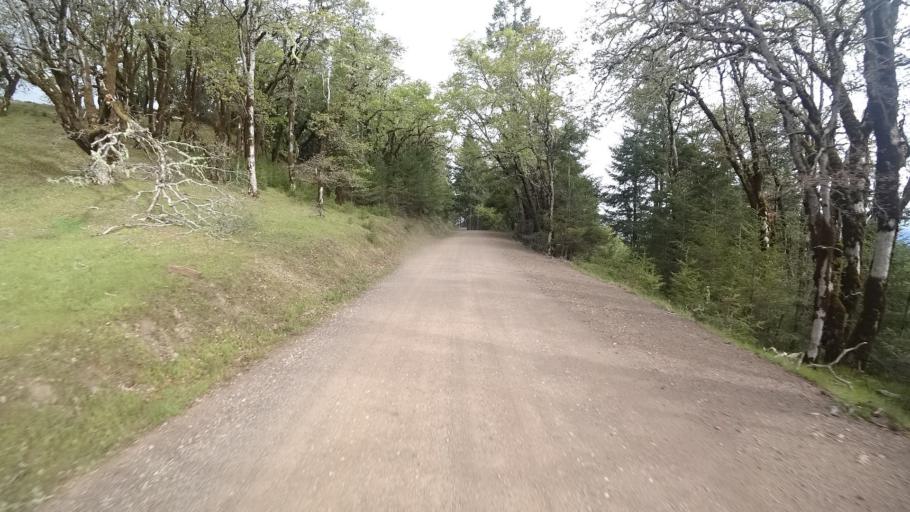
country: US
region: California
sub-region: Humboldt County
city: Redway
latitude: 40.2038
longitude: -123.7165
